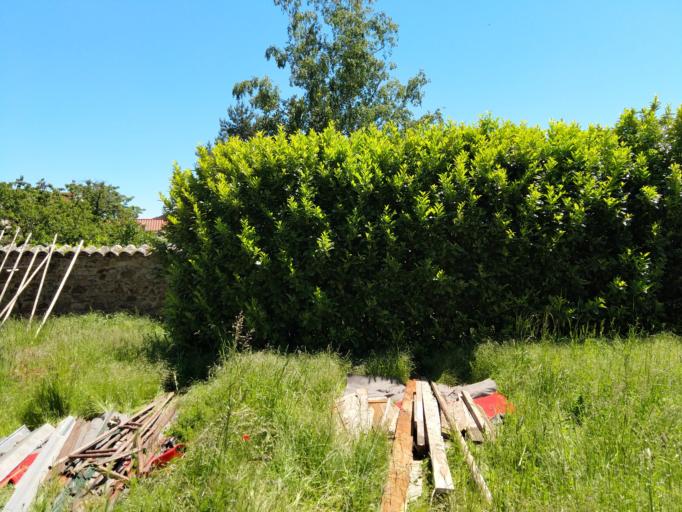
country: FR
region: Rhone-Alpes
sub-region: Departement de la Loire
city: Pelussin
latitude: 45.4172
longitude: 4.6744
